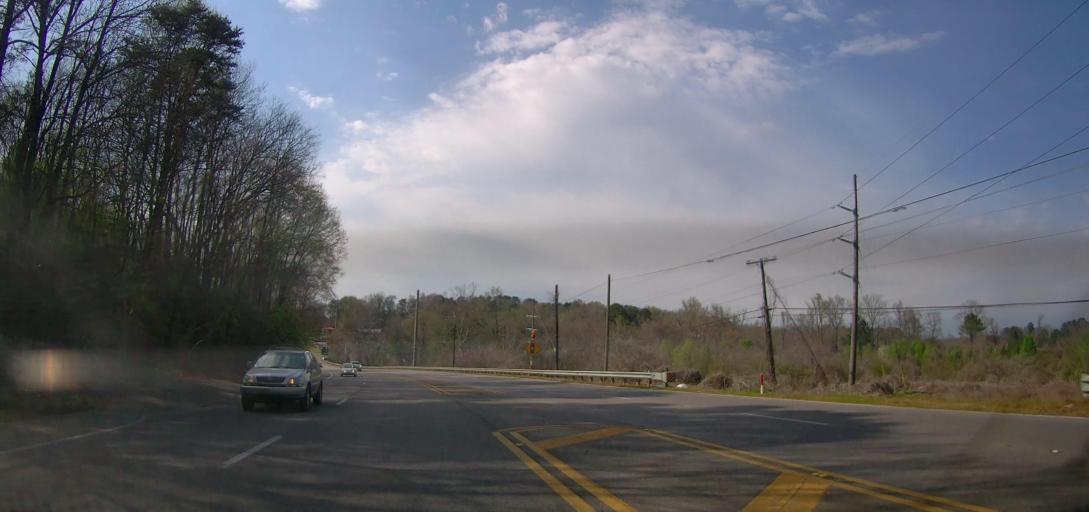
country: US
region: Alabama
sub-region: Jefferson County
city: Forestdale
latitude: 33.5729
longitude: -86.9027
